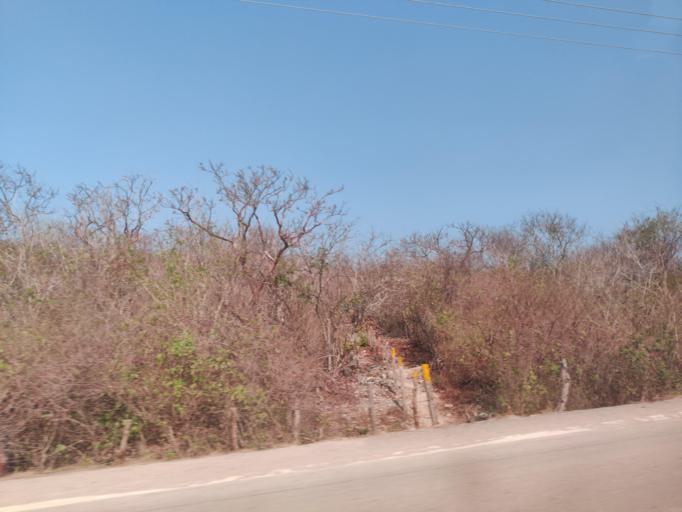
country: CO
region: Bolivar
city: Turbana
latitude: 10.1818
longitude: -75.6447
